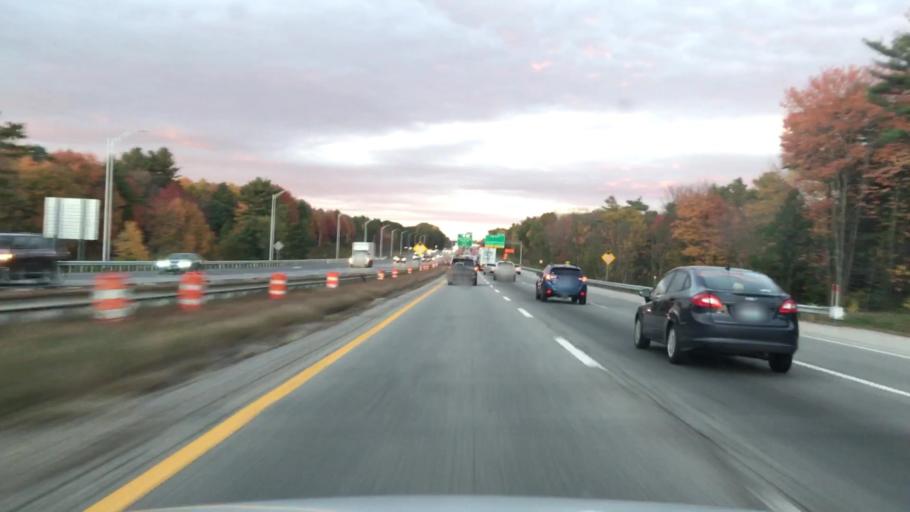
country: US
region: Maine
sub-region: Cumberland County
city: West Scarborough
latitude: 43.6146
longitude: -70.3624
